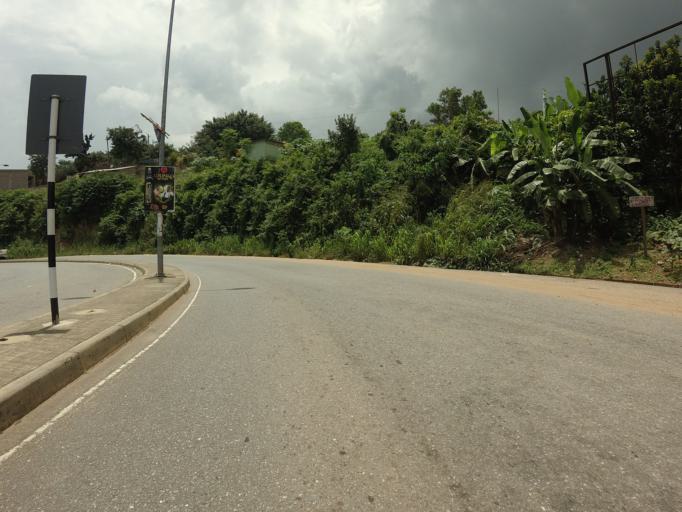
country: GH
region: Eastern
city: Aburi
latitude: 5.8025
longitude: -0.1831
